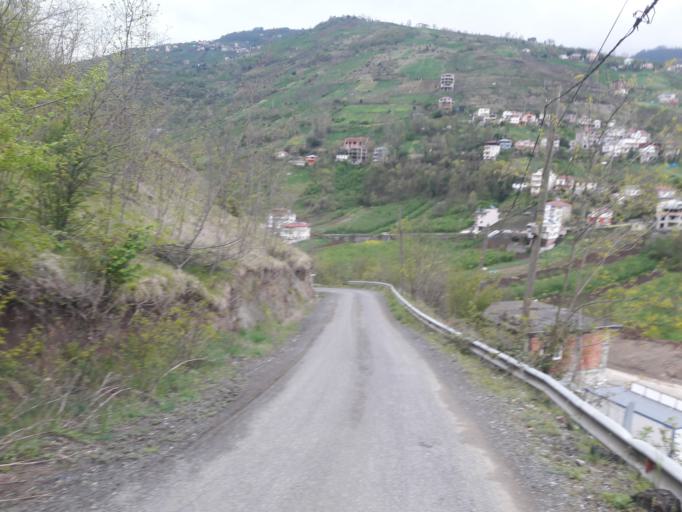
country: TR
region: Trabzon
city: Duzkoy
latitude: 40.9232
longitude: 39.4886
